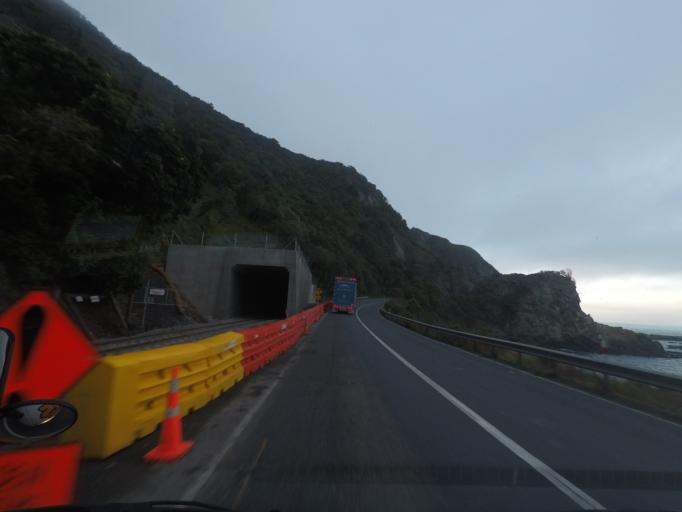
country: NZ
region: Canterbury
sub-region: Kaikoura District
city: Kaikoura
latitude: -42.4501
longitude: 173.5730
